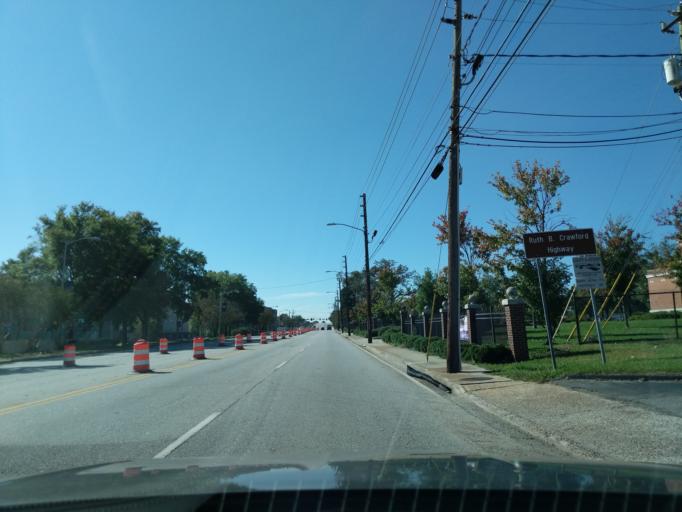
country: US
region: Georgia
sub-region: Richmond County
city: Augusta
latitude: 33.4699
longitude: -81.9921
